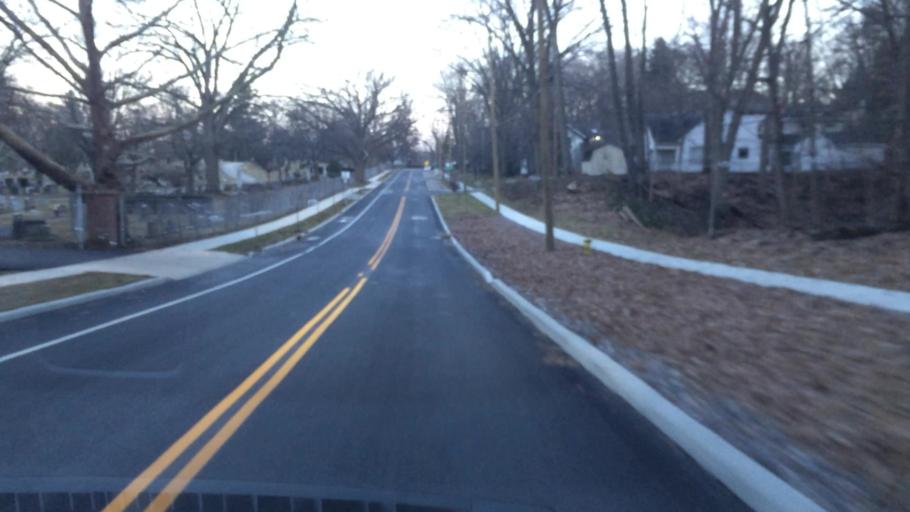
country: US
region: Ohio
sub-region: Summit County
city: Akron
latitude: 41.0984
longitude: -81.5351
